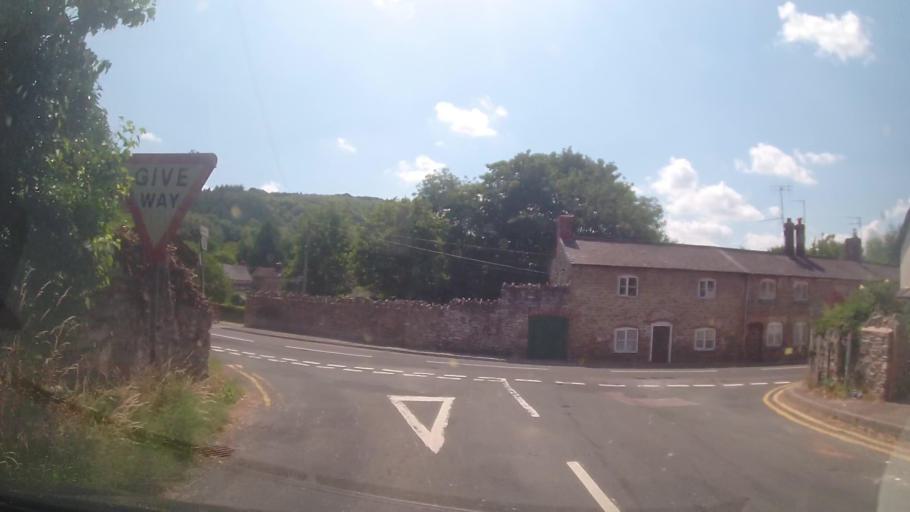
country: GB
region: England
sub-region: Herefordshire
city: Brockhampton
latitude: 52.0334
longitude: -2.6264
